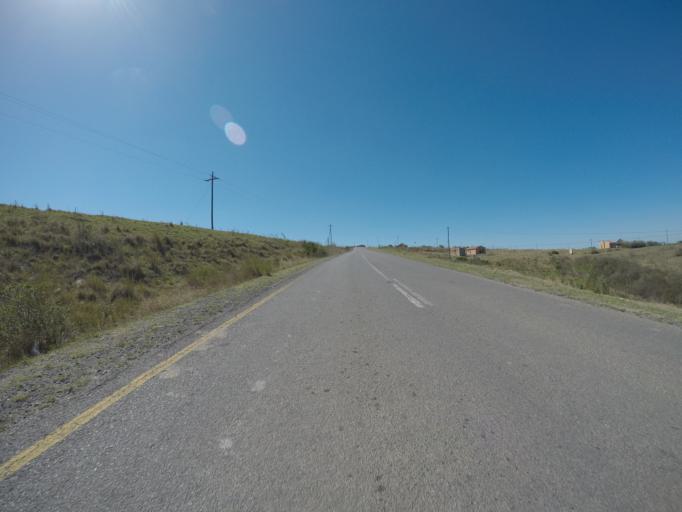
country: ZA
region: Eastern Cape
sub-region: OR Tambo District Municipality
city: Libode
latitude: -31.9105
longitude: 29.0109
